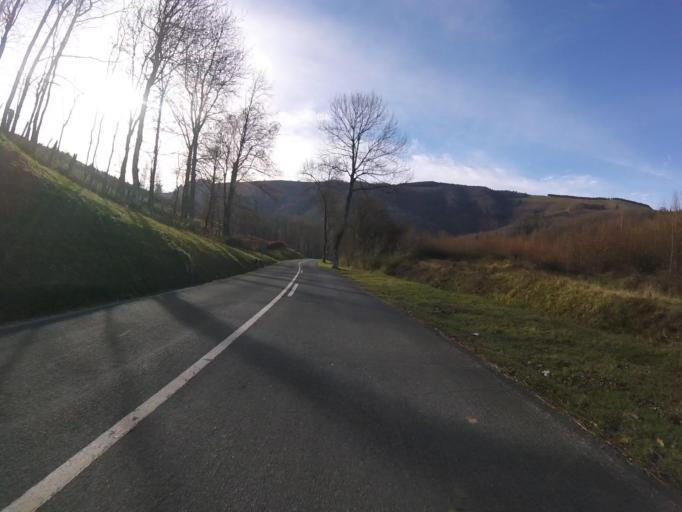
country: ES
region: Navarre
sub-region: Provincia de Navarra
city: Areso
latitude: 43.1004
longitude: -1.9528
